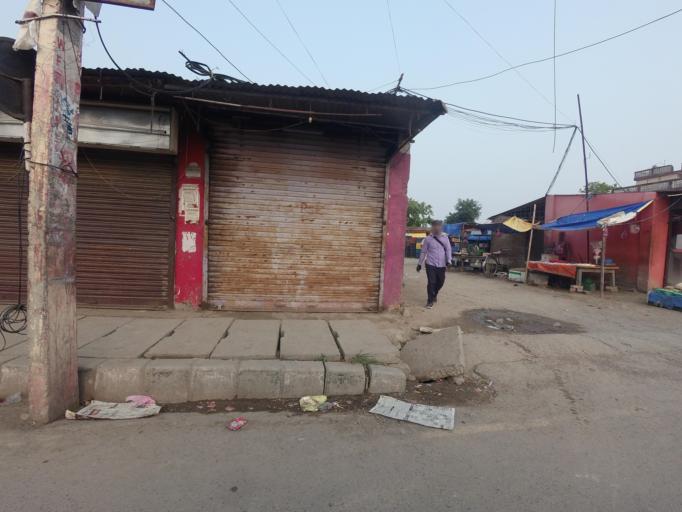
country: NP
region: Western Region
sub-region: Lumbini Zone
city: Bhairahawa
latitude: 27.5166
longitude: 83.4495
